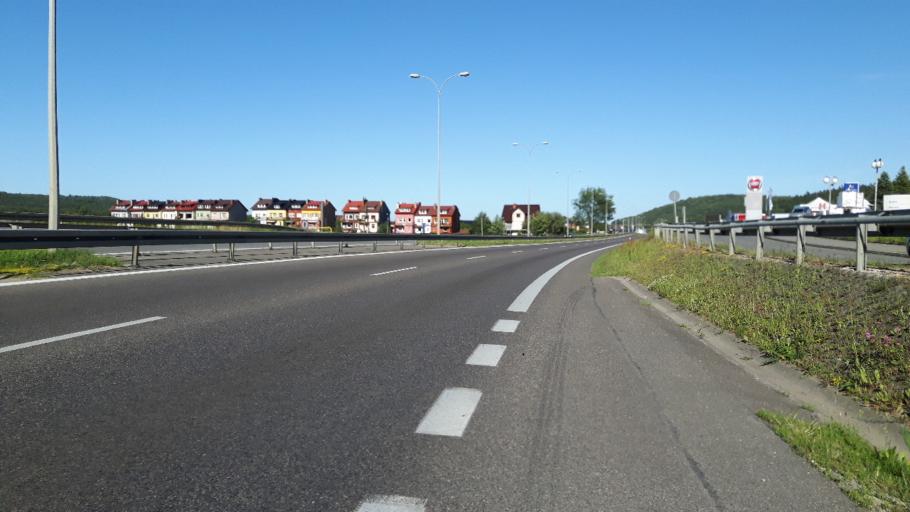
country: PL
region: Pomeranian Voivodeship
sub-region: Powiat wejherowski
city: Wejherowo
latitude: 54.6031
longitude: 18.2912
